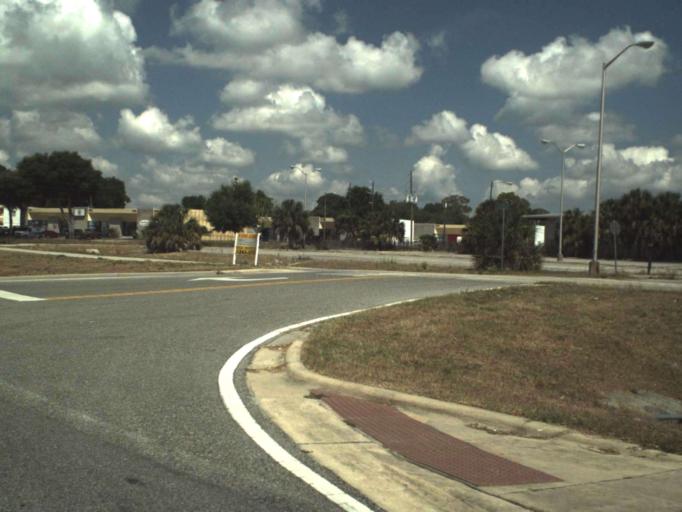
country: US
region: Florida
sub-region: Lake County
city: Eustis
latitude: 28.8221
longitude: -81.6969
